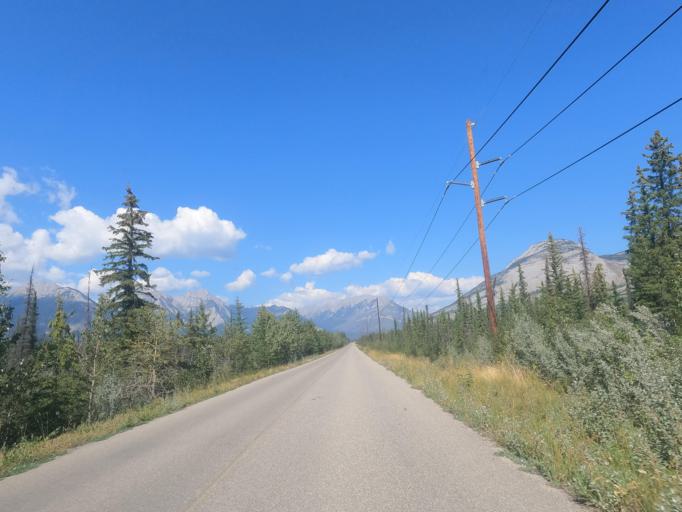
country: CA
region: Alberta
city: Jasper Park Lodge
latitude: 53.0017
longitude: -118.0850
